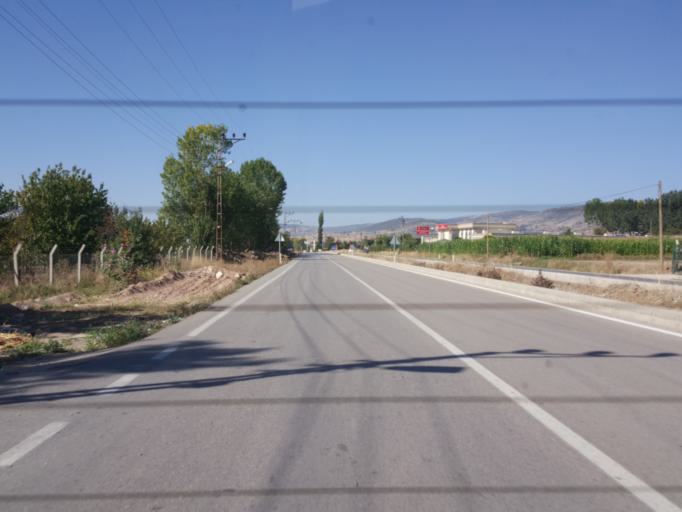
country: TR
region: Tokat
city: Zile
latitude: 40.3101
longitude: 35.9112
